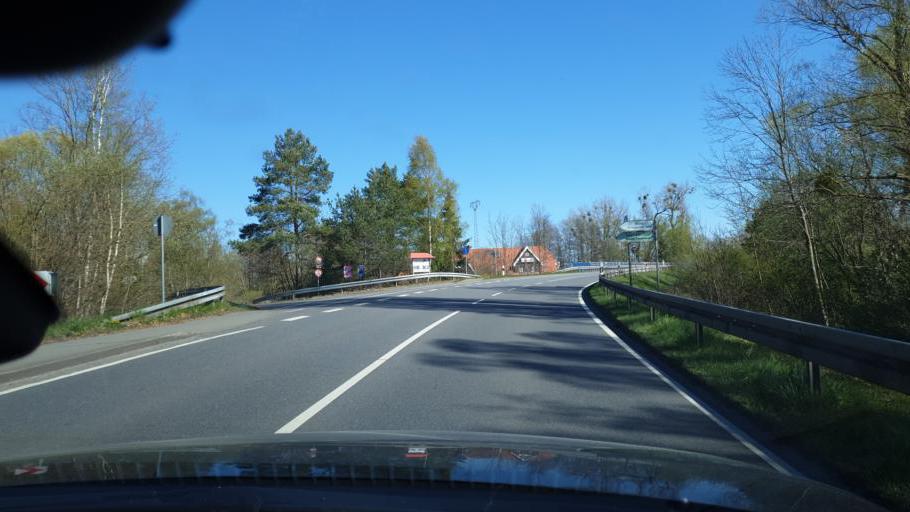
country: DE
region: Mecklenburg-Vorpommern
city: Seehof
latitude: 53.6771
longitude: 11.4495
